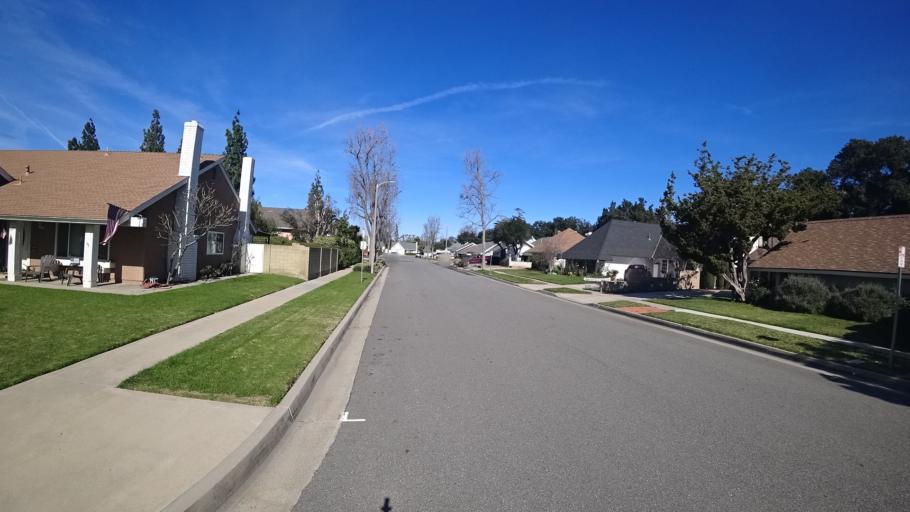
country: US
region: California
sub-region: Orange County
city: Orange
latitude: 33.7678
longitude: -117.8451
